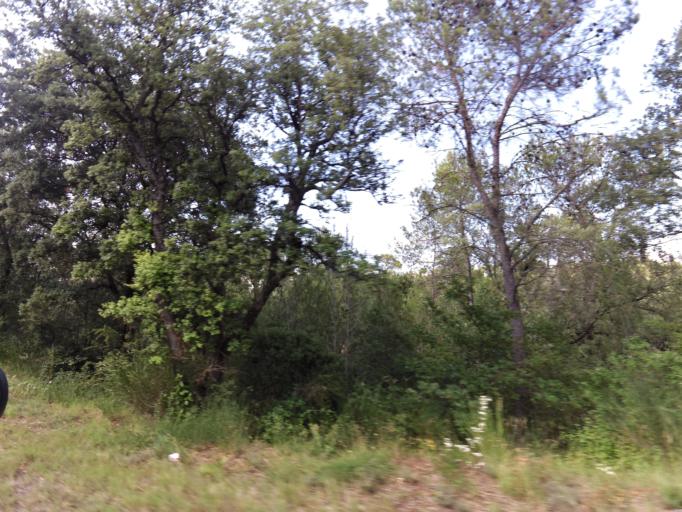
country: FR
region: Languedoc-Roussillon
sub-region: Departement du Gard
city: Sommieres
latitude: 43.8254
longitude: 4.0503
